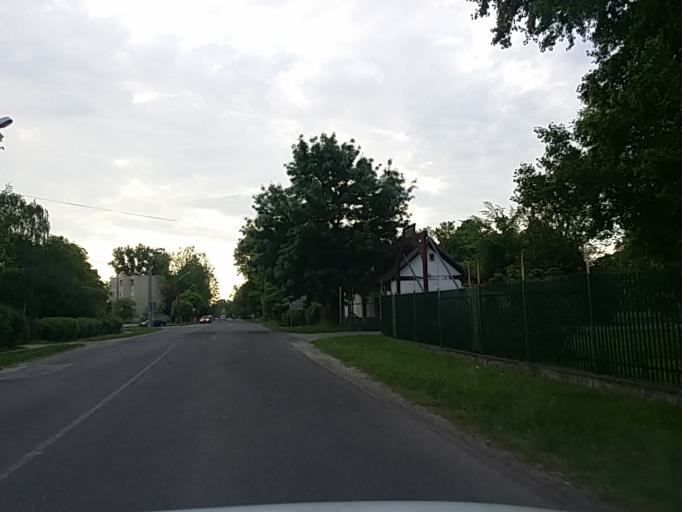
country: HU
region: Bacs-Kiskun
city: Kecskemet
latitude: 46.8978
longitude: 19.7188
